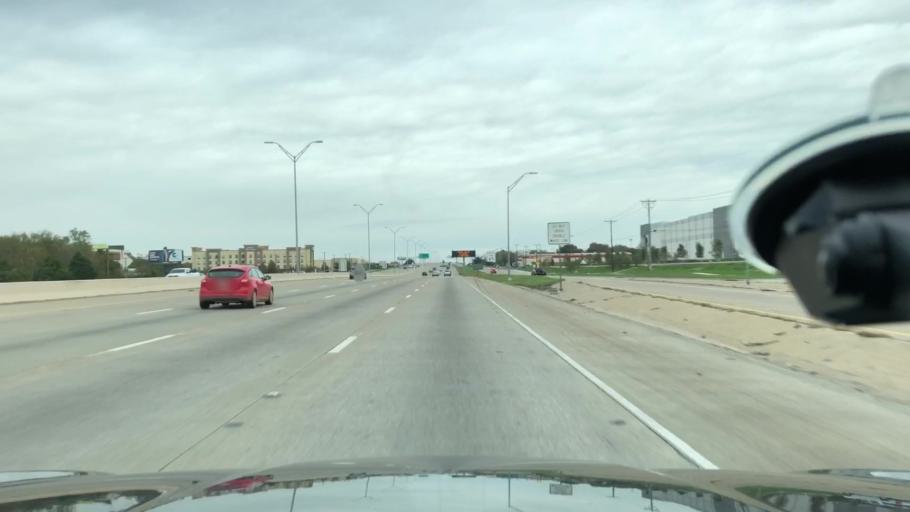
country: US
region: Texas
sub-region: Dallas County
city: DeSoto
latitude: 32.6221
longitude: -96.8229
